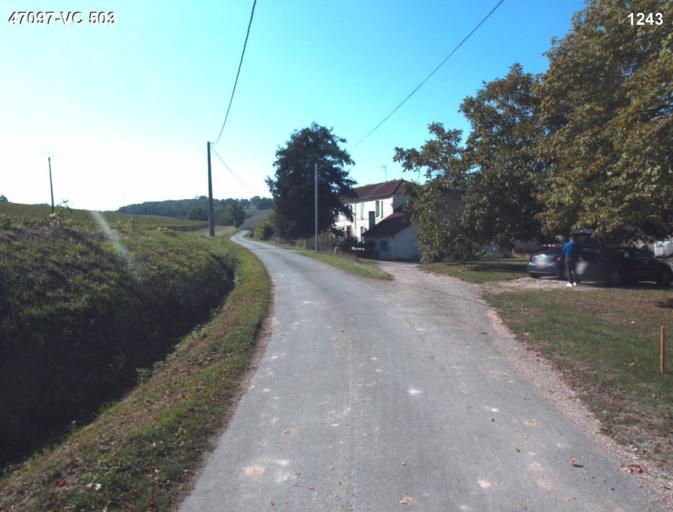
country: FR
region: Aquitaine
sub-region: Departement du Lot-et-Garonne
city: Vianne
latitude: 44.2027
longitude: 0.3720
